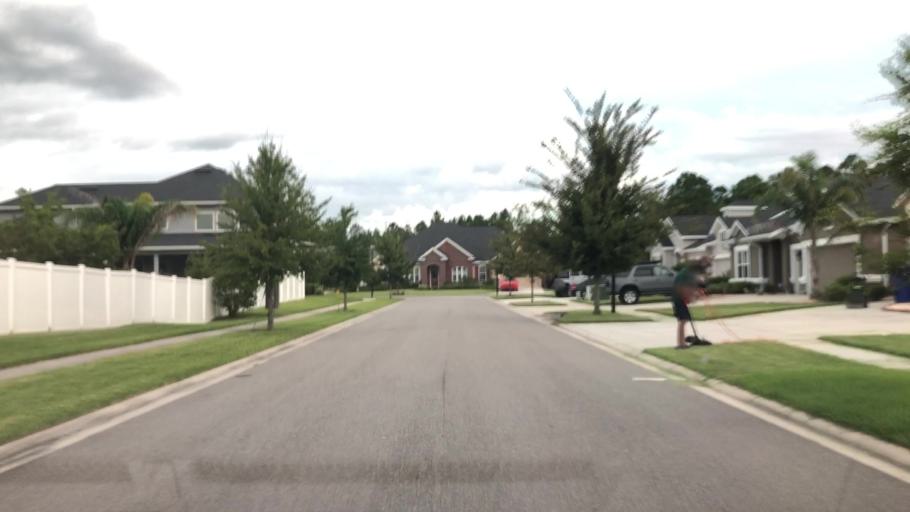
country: US
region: Florida
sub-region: Saint Johns County
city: Palm Valley
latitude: 30.0945
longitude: -81.4639
